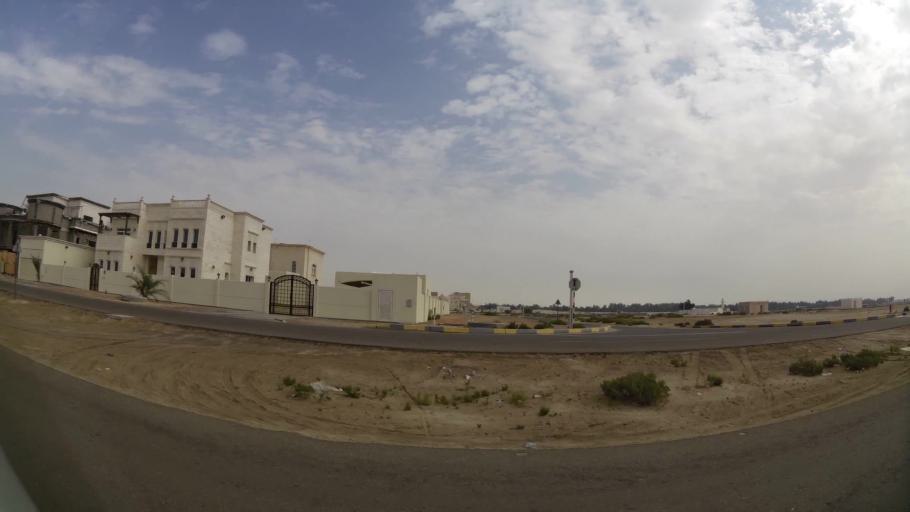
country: AE
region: Abu Dhabi
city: Abu Dhabi
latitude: 24.3050
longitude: 54.6570
